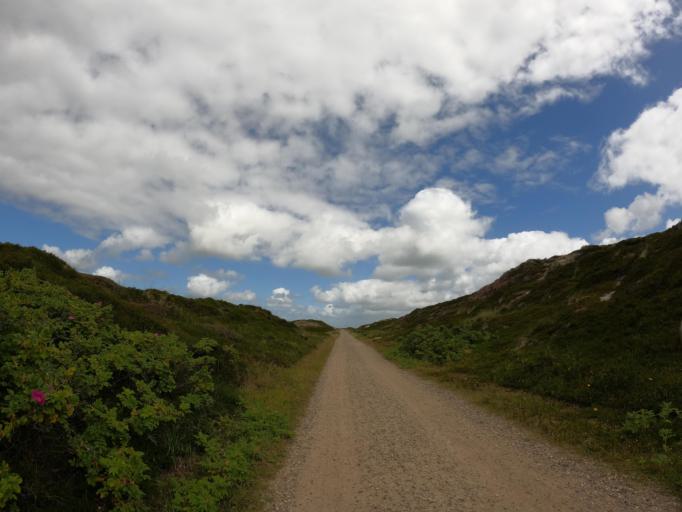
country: DE
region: Schleswig-Holstein
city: Norddorf
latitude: 54.7830
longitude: 8.2876
